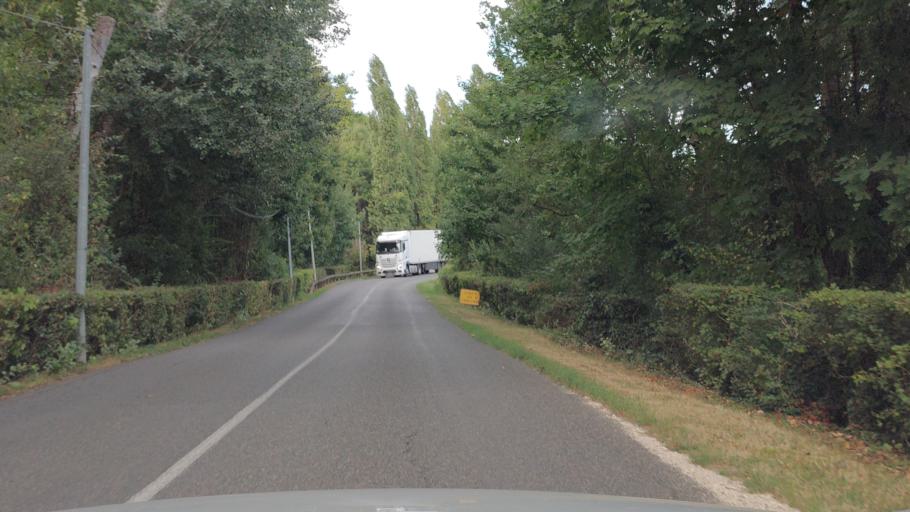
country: FR
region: Ile-de-France
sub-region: Departement de Seine-et-Marne
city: La Chapelle-Gauthier
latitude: 48.5574
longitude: 2.8764
